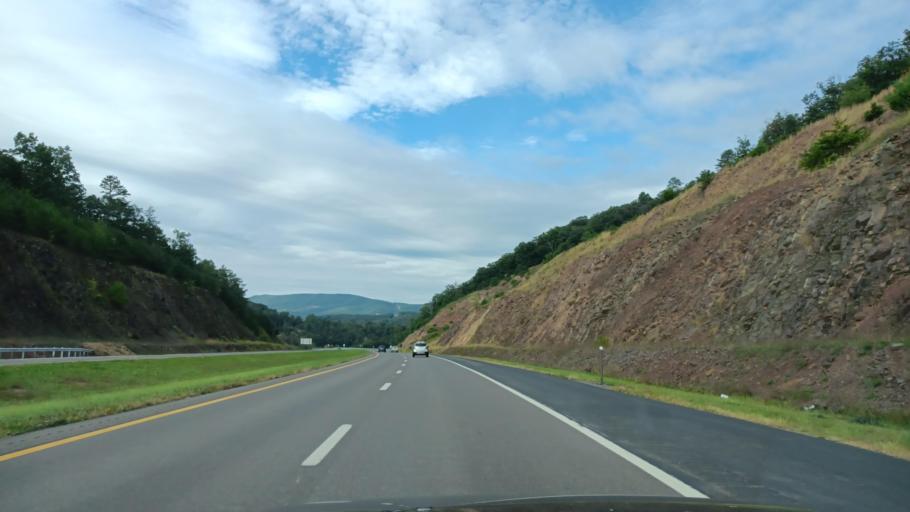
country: US
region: West Virginia
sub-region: Hardy County
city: Moorefield
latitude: 39.0519
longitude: -78.7652
